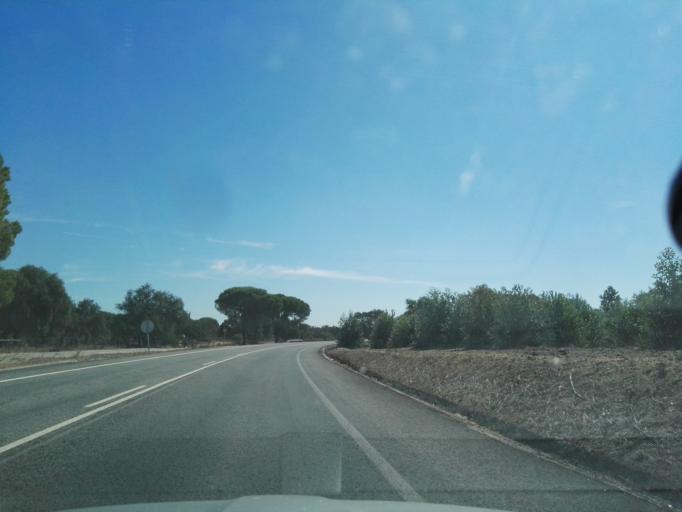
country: PT
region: Santarem
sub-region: Benavente
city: Poceirao
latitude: 38.8671
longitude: -8.7887
